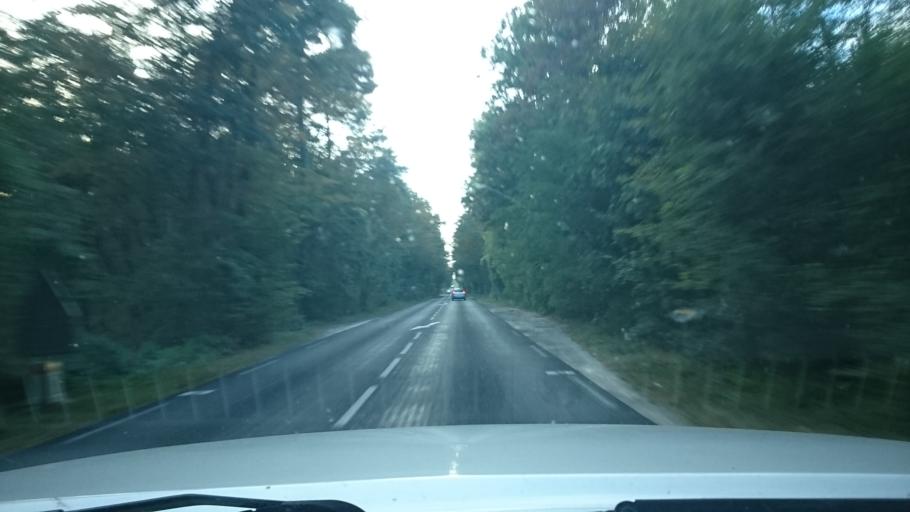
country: FR
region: Ile-de-France
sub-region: Departement de Seine-et-Marne
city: Samoreau
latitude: 48.4355
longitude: 2.7363
